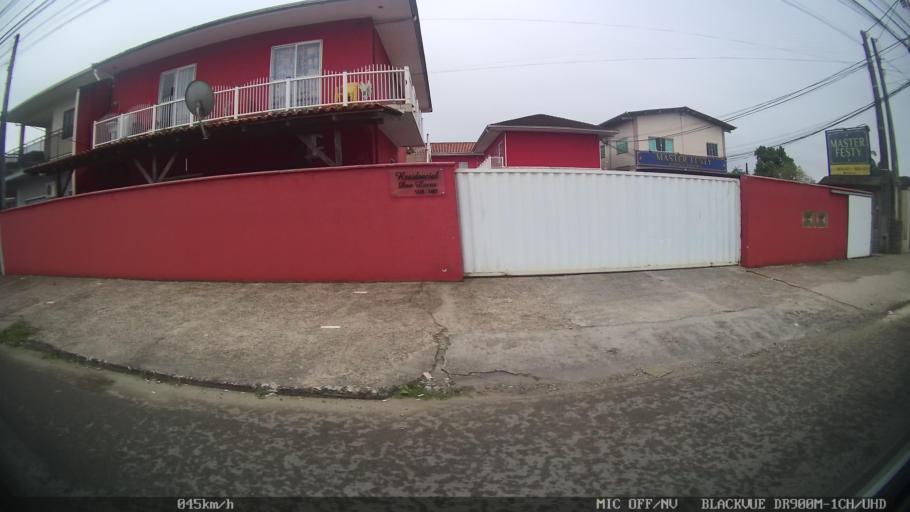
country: BR
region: Santa Catarina
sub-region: Joinville
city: Joinville
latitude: -26.2613
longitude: -48.8108
